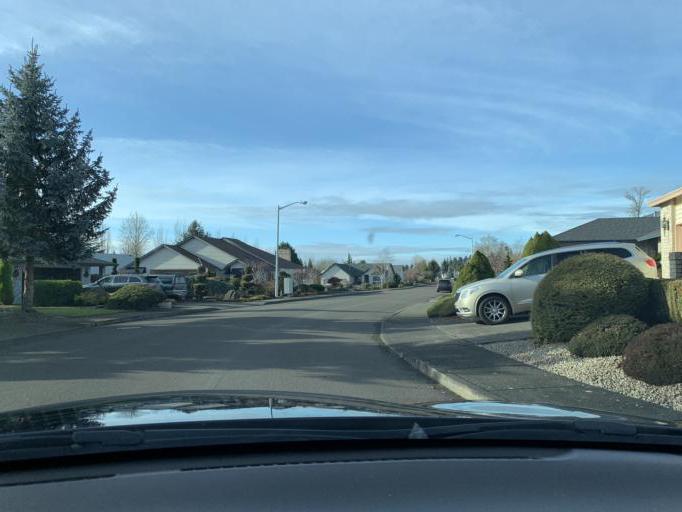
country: US
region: Washington
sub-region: Clark County
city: Mill Plain
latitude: 45.5954
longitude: -122.5127
